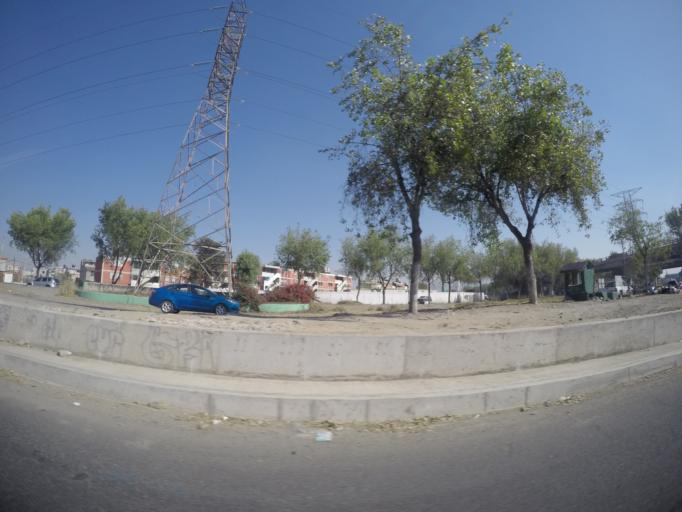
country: MX
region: Mexico
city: Santo Tomas Chiconautla
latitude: 19.6129
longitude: -99.0086
